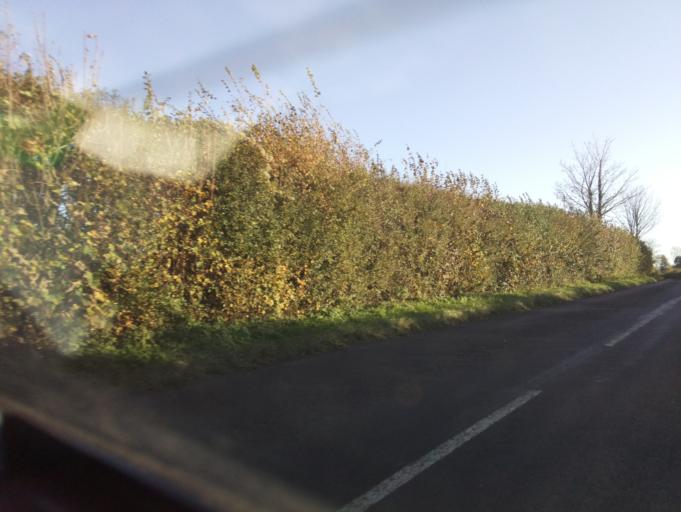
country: GB
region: England
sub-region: Somerset
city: Milborne Port
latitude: 50.9786
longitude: -2.4626
